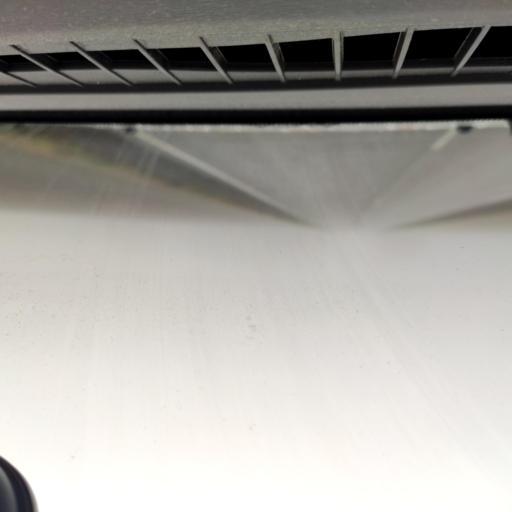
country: RU
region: Belgorod
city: Ilovka
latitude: 50.7604
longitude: 38.7367
